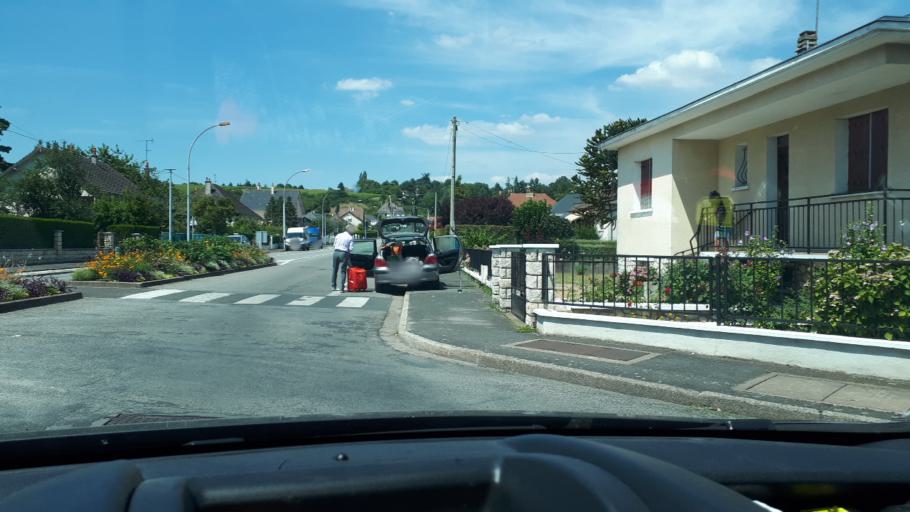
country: FR
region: Centre
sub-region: Departement du Loir-et-Cher
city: Vendome
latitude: 47.8056
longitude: 1.0542
